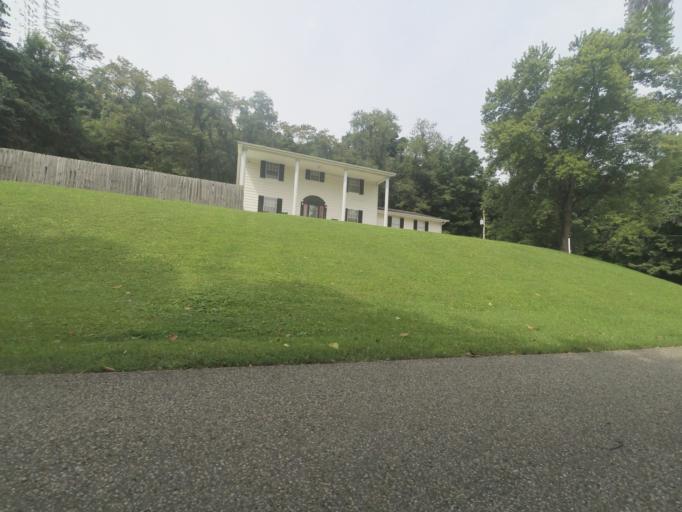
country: US
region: West Virginia
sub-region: Cabell County
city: Huntington
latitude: 38.4345
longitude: -82.4676
